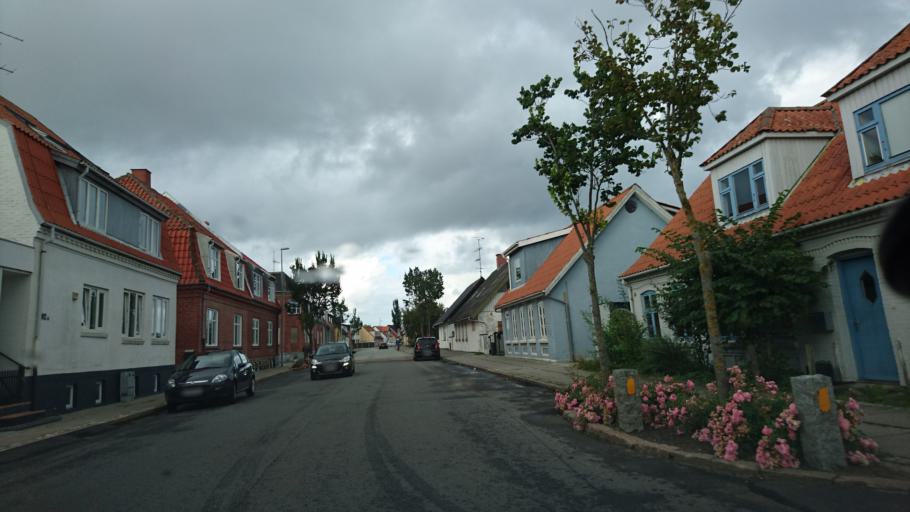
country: DK
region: North Denmark
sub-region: Frederikshavn Kommune
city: Frederikshavn
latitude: 57.4314
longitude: 10.5253
